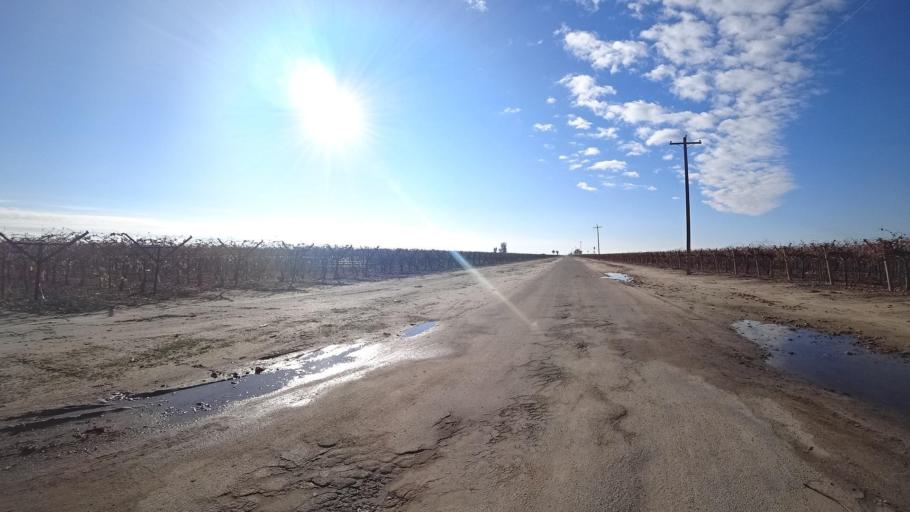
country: US
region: California
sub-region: Kern County
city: Delano
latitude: 35.7322
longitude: -119.2941
